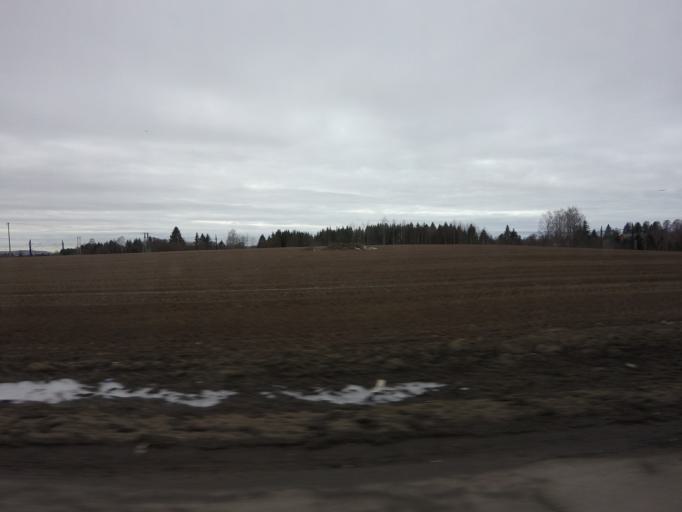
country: NO
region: Akershus
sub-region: Ullensaker
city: Jessheim
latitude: 60.1447
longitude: 11.1518
